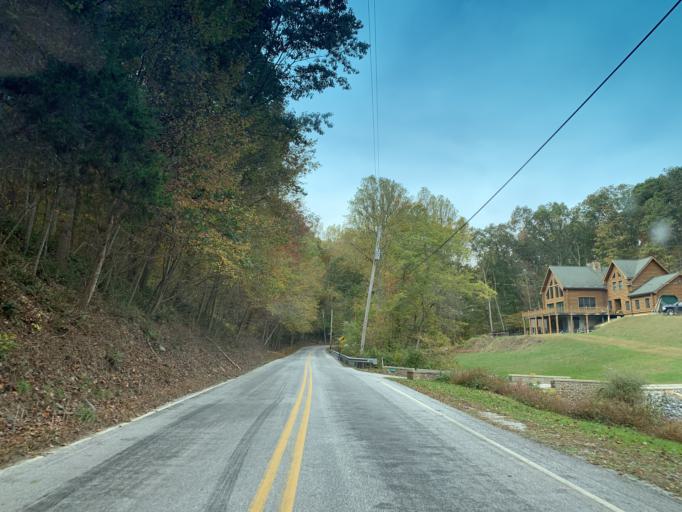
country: US
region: Pennsylvania
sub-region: York County
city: Stewartstown
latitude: 39.8300
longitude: -76.5121
